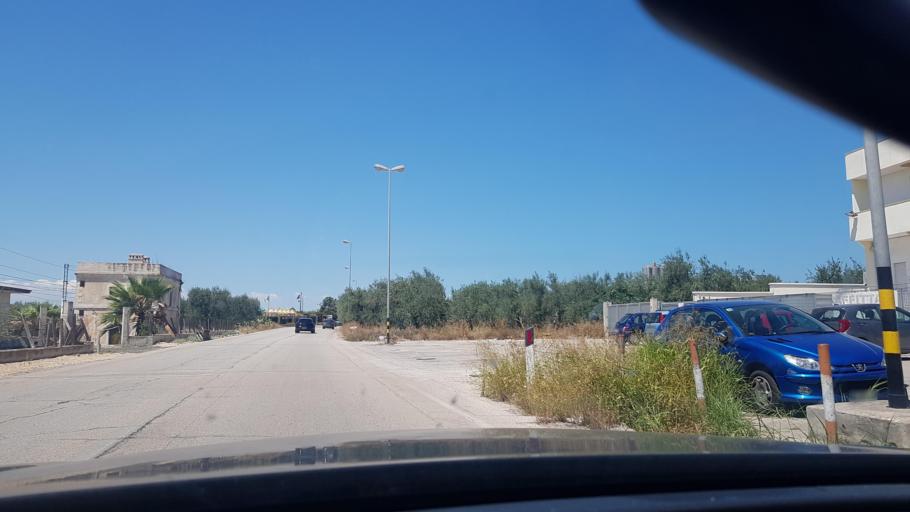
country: IT
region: Apulia
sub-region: Provincia di Barletta - Andria - Trani
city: Barletta
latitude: 41.3027
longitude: 16.3237
